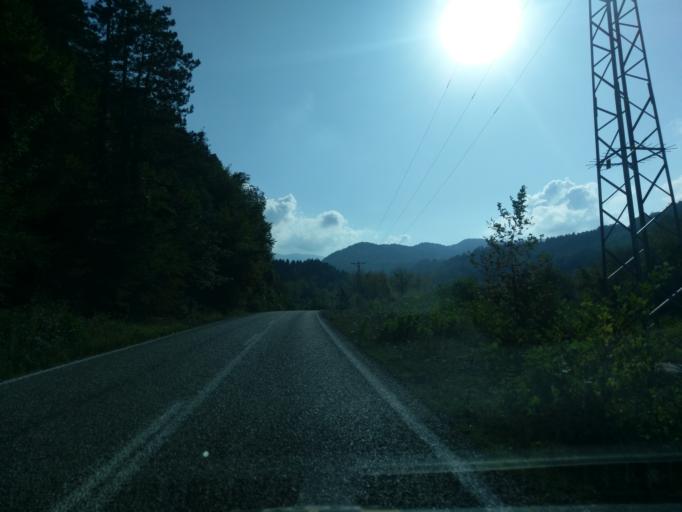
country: TR
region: Sinop
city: Yenikonak
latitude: 41.8800
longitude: 34.5572
